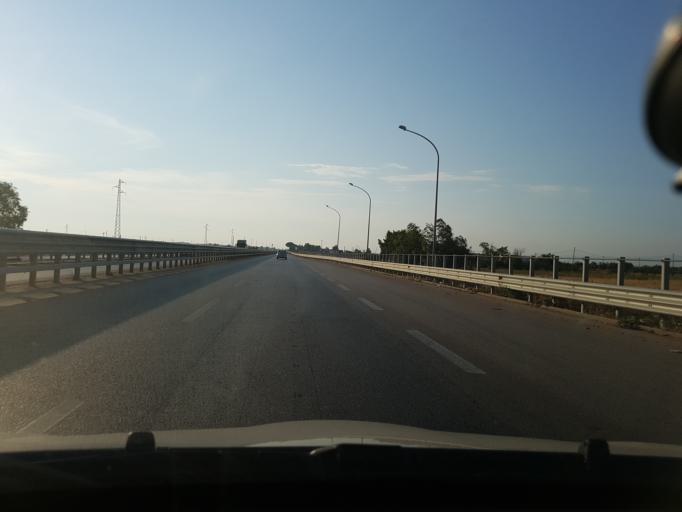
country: IT
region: Apulia
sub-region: Provincia di Foggia
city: Carapelle
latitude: 41.3746
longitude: 15.6849
